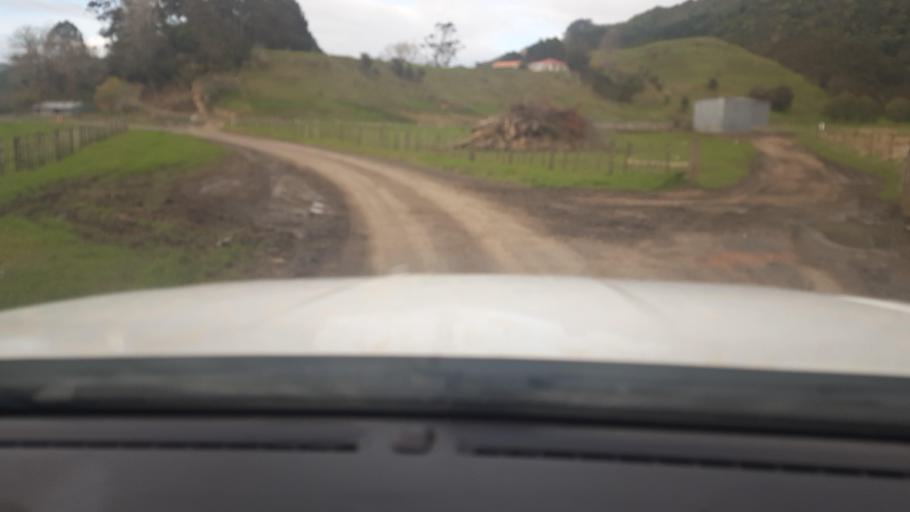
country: NZ
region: Northland
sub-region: Far North District
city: Ahipara
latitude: -35.2611
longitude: 173.1980
